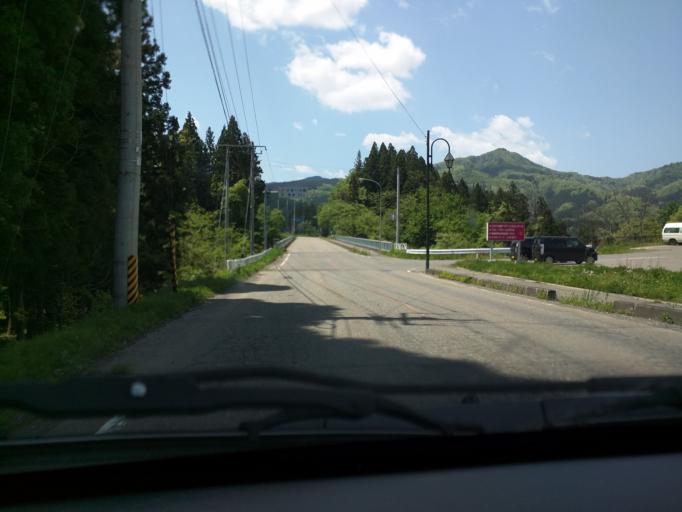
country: JP
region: Fukushima
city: Kitakata
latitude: 37.5969
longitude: 139.6386
